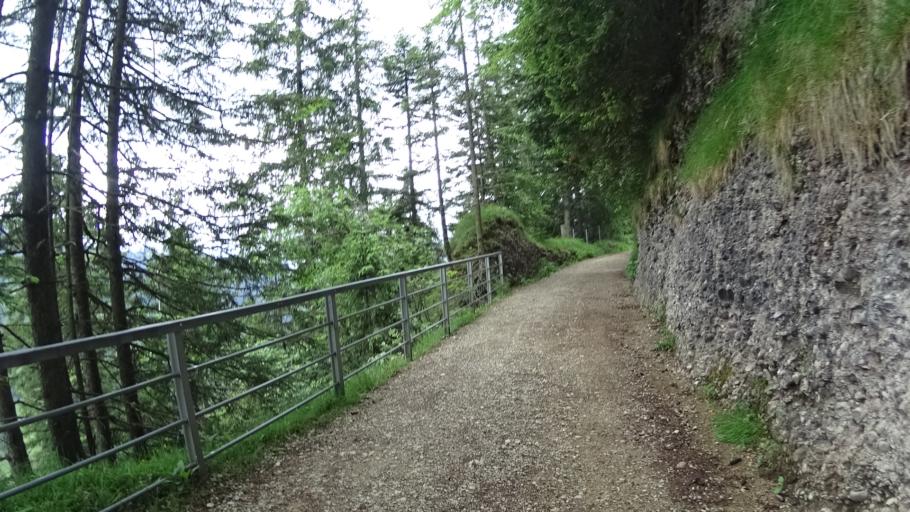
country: CH
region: Lucerne
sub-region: Lucerne-Land District
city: Vitznau
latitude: 47.0437
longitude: 8.4795
